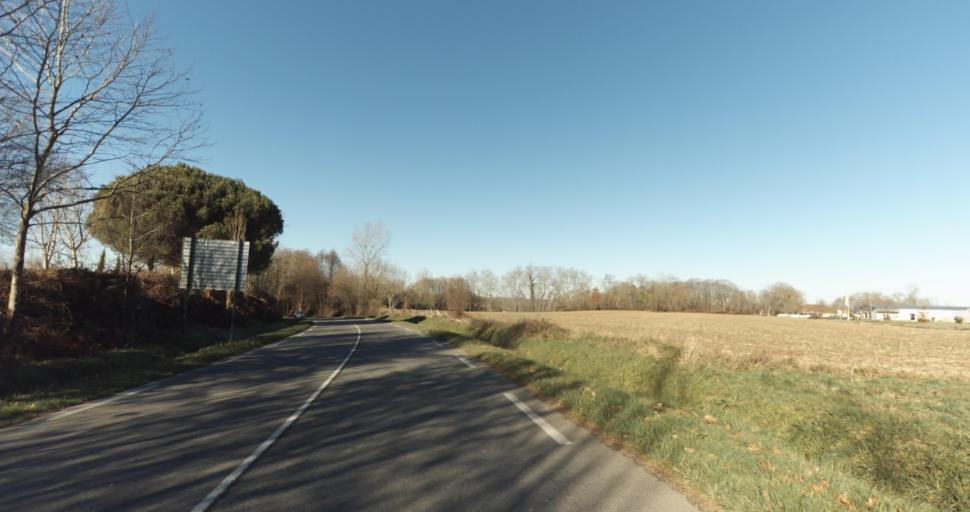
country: FR
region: Aquitaine
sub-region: Departement des Pyrenees-Atlantiques
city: Morlaas
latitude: 43.3515
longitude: -0.2582
